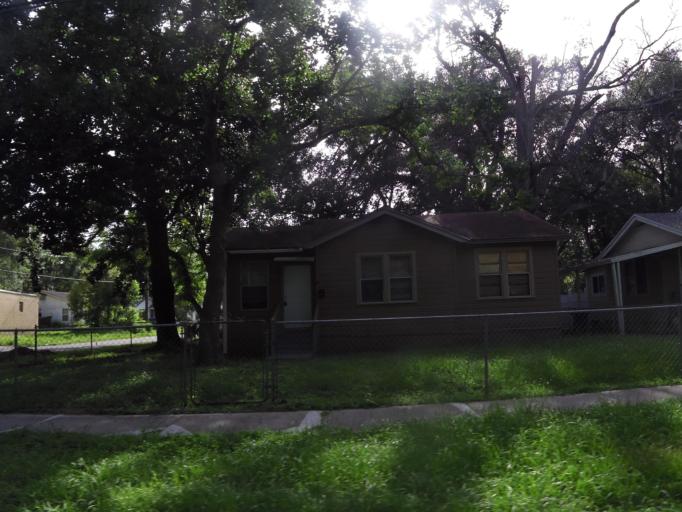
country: US
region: Florida
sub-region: Duval County
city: Jacksonville
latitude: 30.3039
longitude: -81.7221
